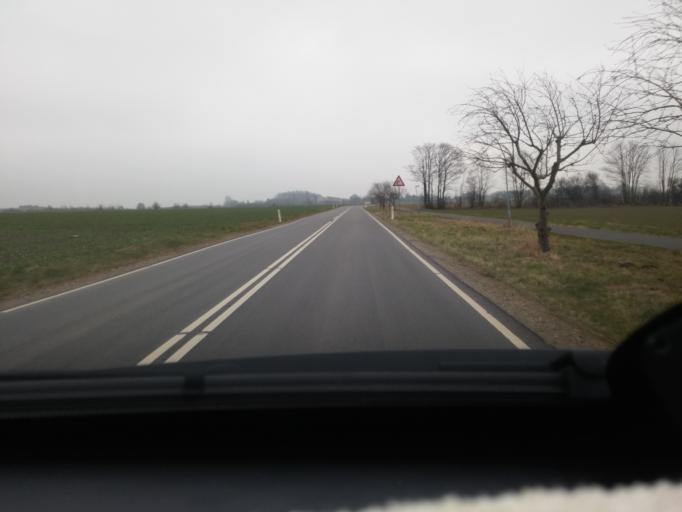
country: DK
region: South Denmark
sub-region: Nyborg Kommune
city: Ullerslev
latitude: 55.3772
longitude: 10.7262
